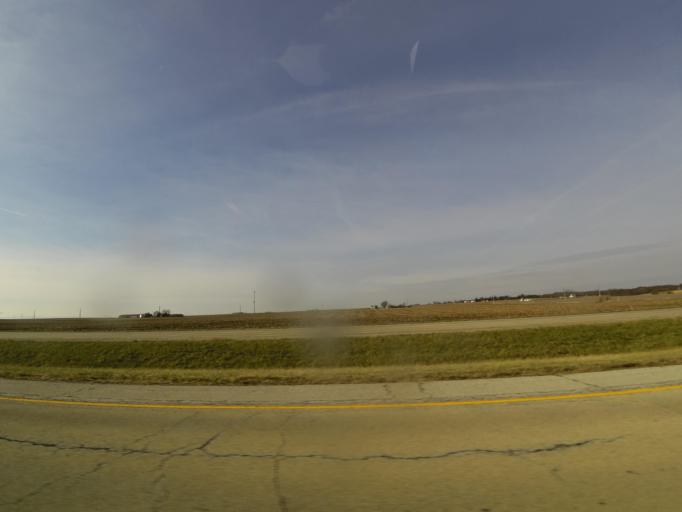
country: US
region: Illinois
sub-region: Macon County
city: Maroa
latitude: 40.0799
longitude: -88.9657
